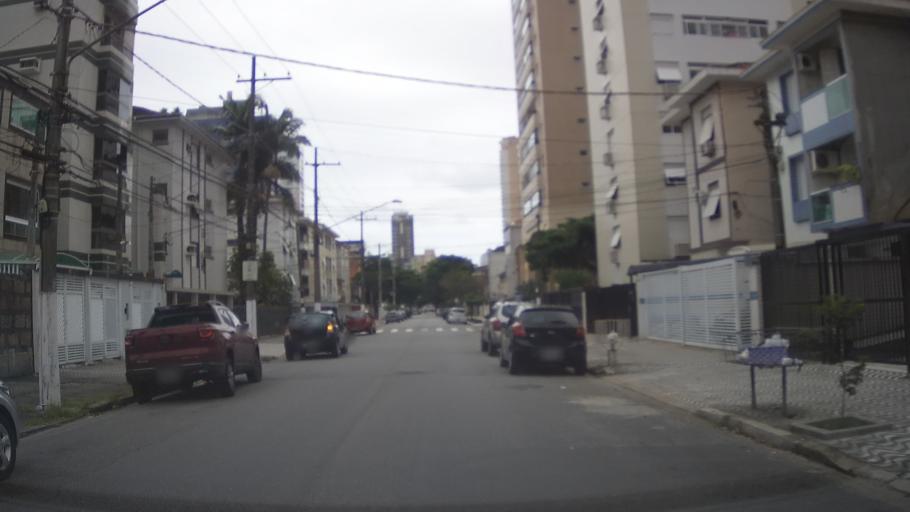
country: BR
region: Sao Paulo
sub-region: Santos
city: Santos
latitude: -23.9690
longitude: -46.3154
